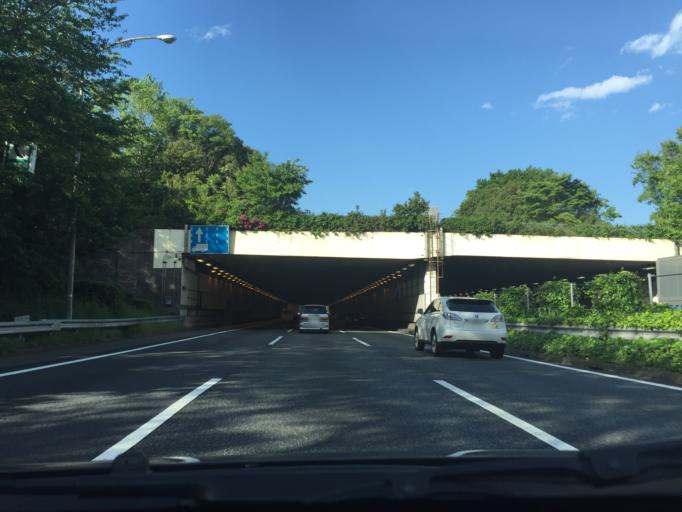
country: JP
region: Kanagawa
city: Minami-rinkan
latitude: 35.4748
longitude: 139.4489
